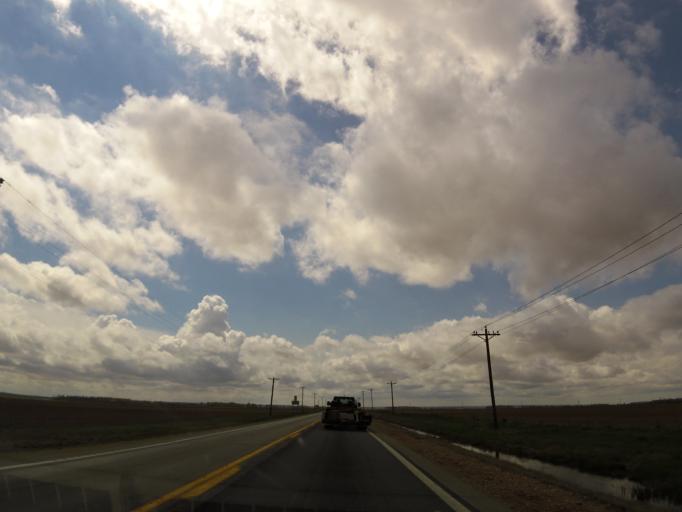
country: US
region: Arkansas
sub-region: Clay County
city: Corning
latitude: 36.3344
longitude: -90.5251
